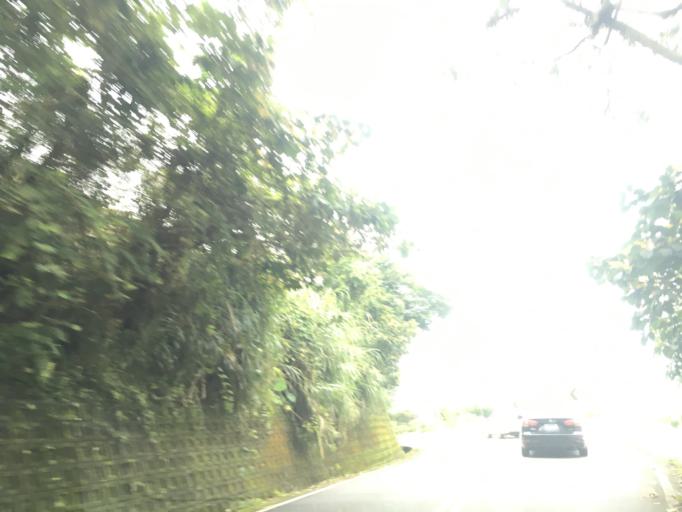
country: TW
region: Taiwan
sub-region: Yunlin
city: Douliu
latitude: 23.5629
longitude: 120.5921
